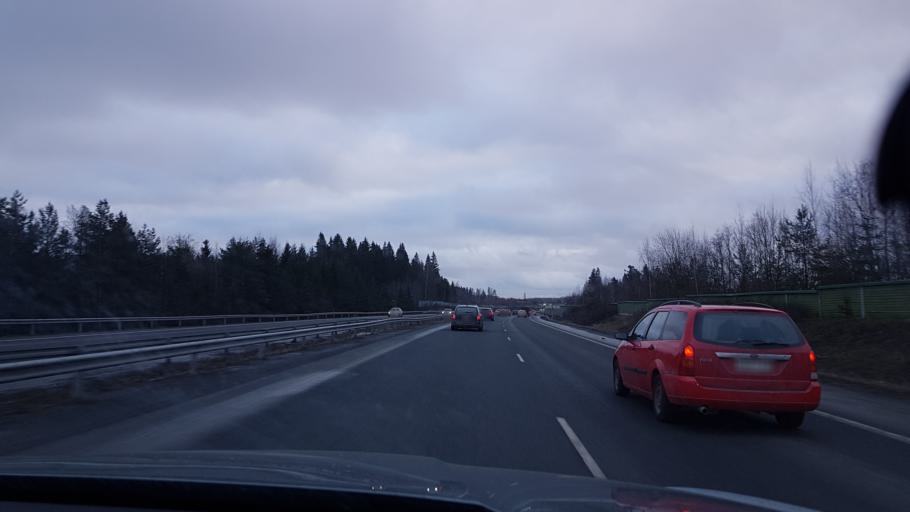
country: FI
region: Pirkanmaa
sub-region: Tampere
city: Lempaeaelae
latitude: 61.3818
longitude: 23.7912
